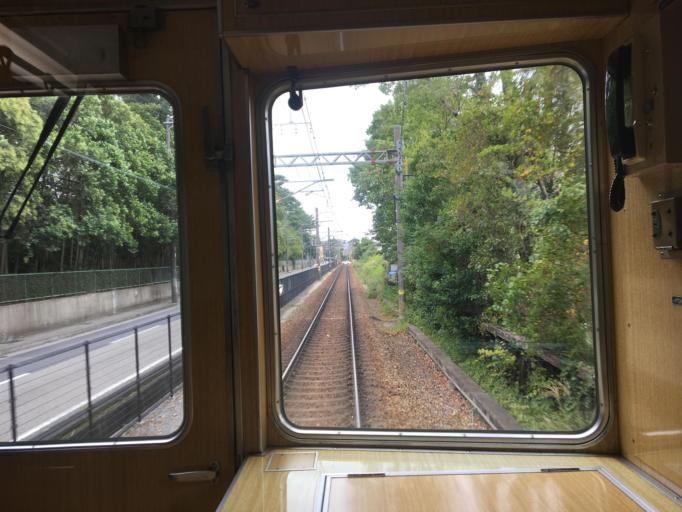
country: JP
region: Hyogo
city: Ashiya
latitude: 34.7561
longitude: 135.3317
